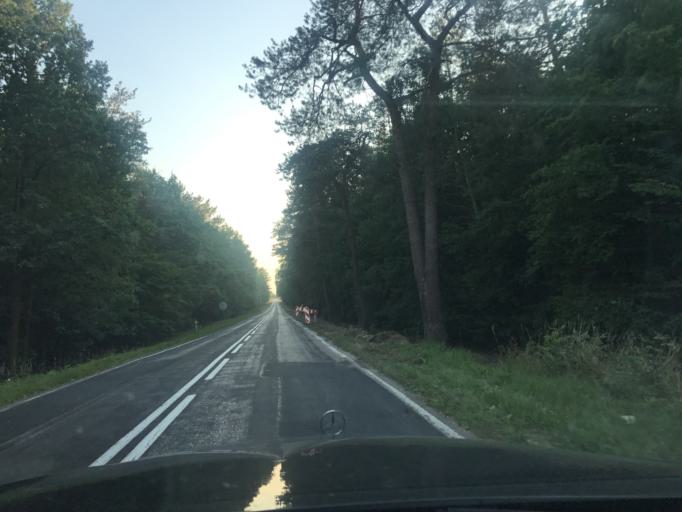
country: PL
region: Lublin Voivodeship
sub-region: Powiat parczewski
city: Siemien
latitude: 51.6091
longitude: 22.7362
